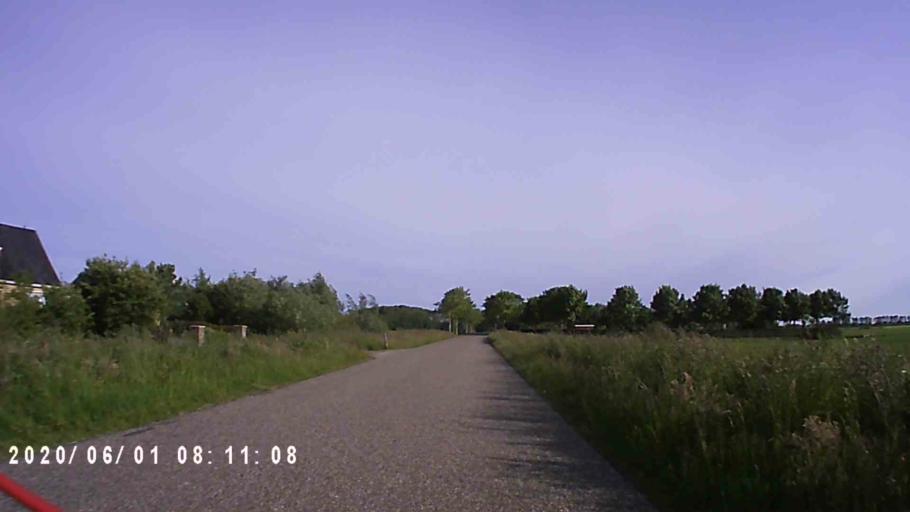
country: NL
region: Friesland
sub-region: Gemeente Ferwerderadiel
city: Burdaard
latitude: 53.2877
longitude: 5.8839
